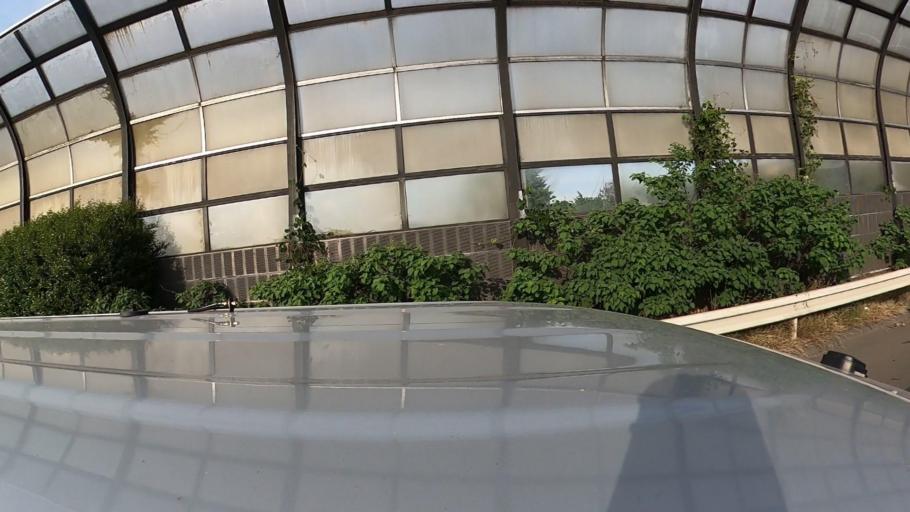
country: JP
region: Saitama
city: Asaka
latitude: 35.7718
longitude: 139.5711
